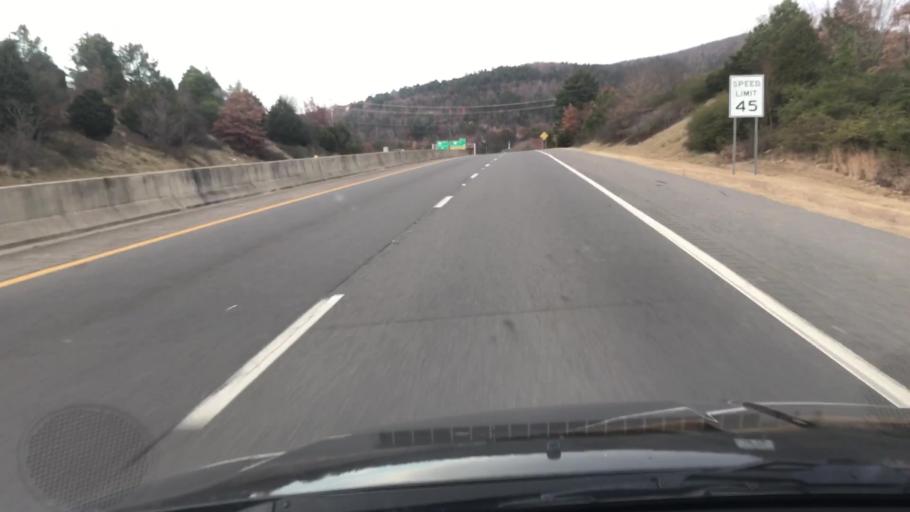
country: US
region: Arkansas
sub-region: Garland County
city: Piney
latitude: 34.4879
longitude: -93.1118
